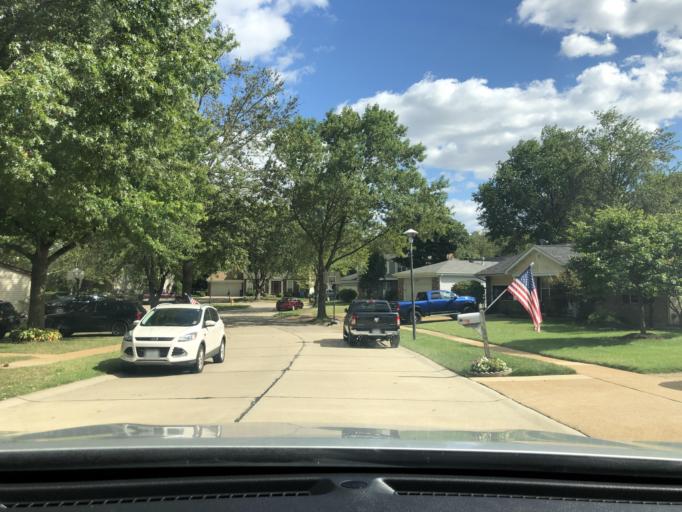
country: US
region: Missouri
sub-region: Saint Louis County
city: Concord
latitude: 38.4979
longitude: -90.3543
